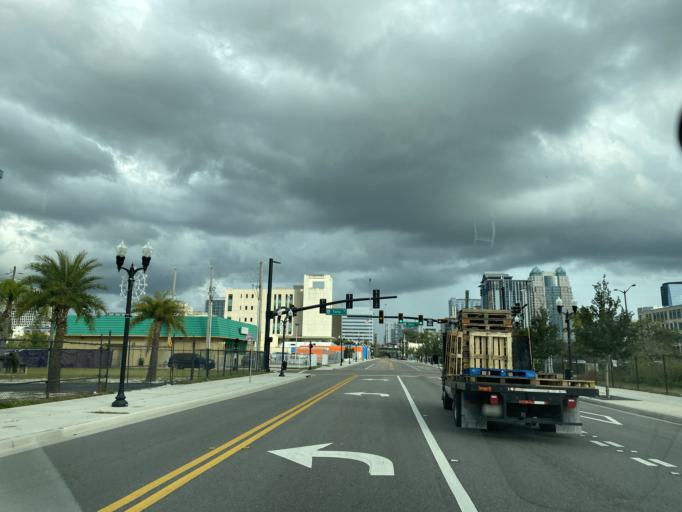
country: US
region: Florida
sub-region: Orange County
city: Orlando
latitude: 28.5420
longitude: -81.3876
